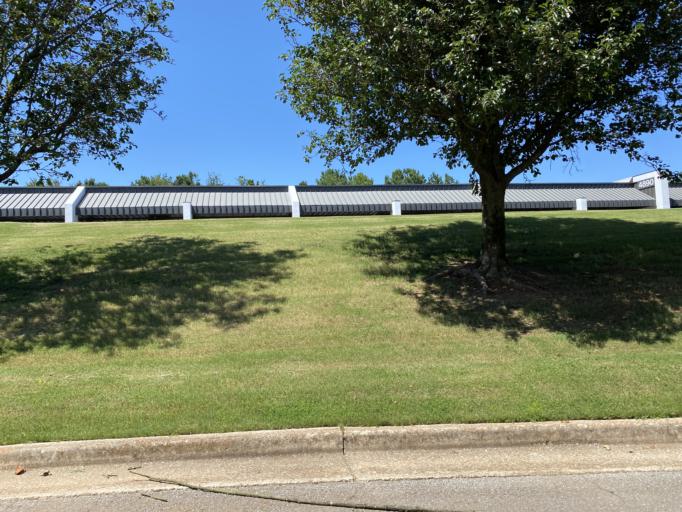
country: US
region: Alabama
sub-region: Madison County
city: Redstone Arsenal
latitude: 34.7432
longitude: -86.6543
